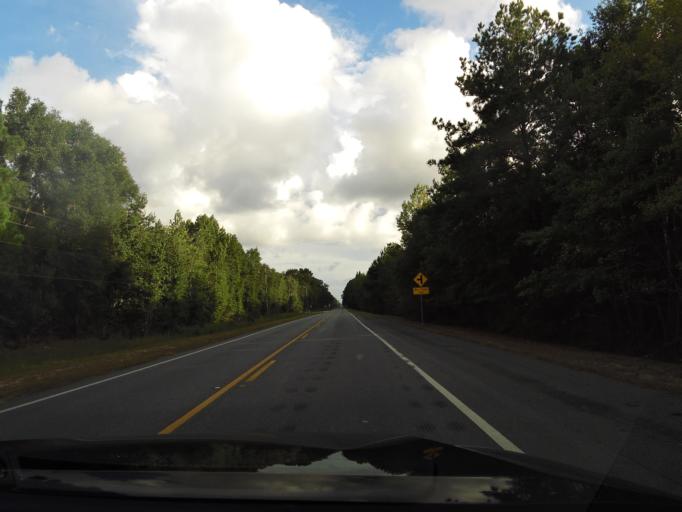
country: US
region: Georgia
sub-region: Liberty County
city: Midway
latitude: 31.7013
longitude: -81.4133
